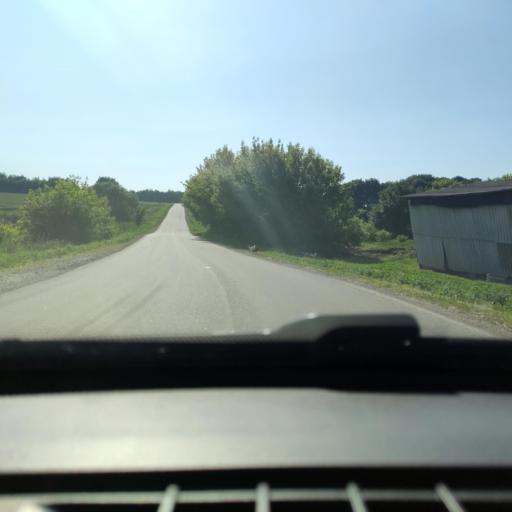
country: RU
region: Voronezj
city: Pereleshinskiy
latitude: 51.6450
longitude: 40.3023
